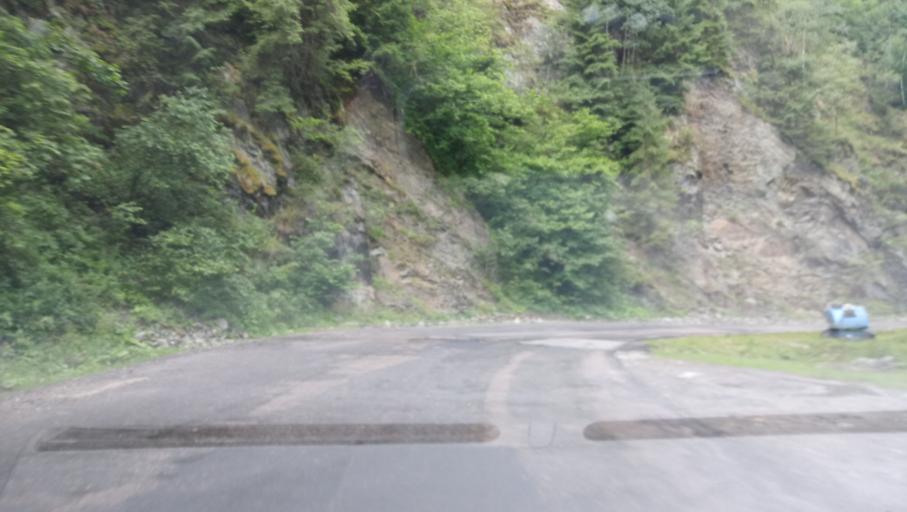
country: RO
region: Hunedoara
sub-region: Oras Petrila
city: Petrila
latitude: 45.4121
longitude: 23.4738
